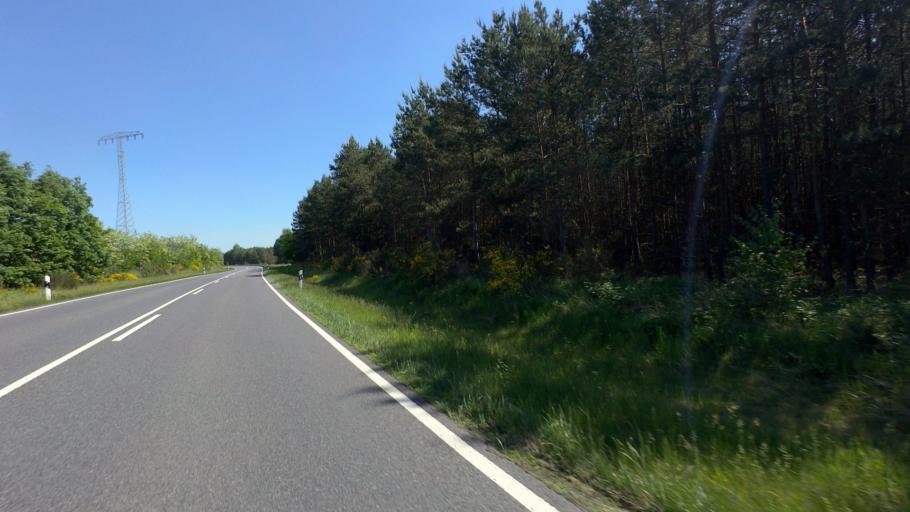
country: DE
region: Brandenburg
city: Spremberg
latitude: 51.5627
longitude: 14.3273
